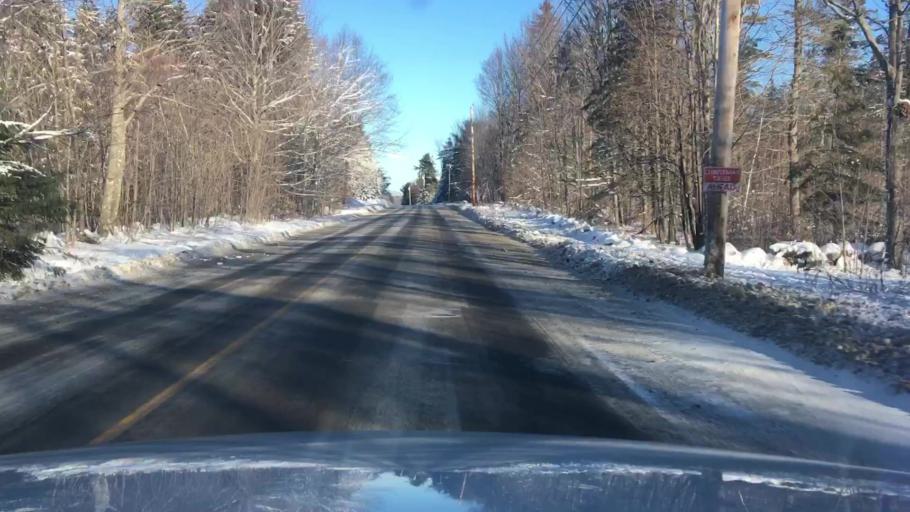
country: US
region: Maine
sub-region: Kennebec County
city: Mount Vernon
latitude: 44.4540
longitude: -69.9707
